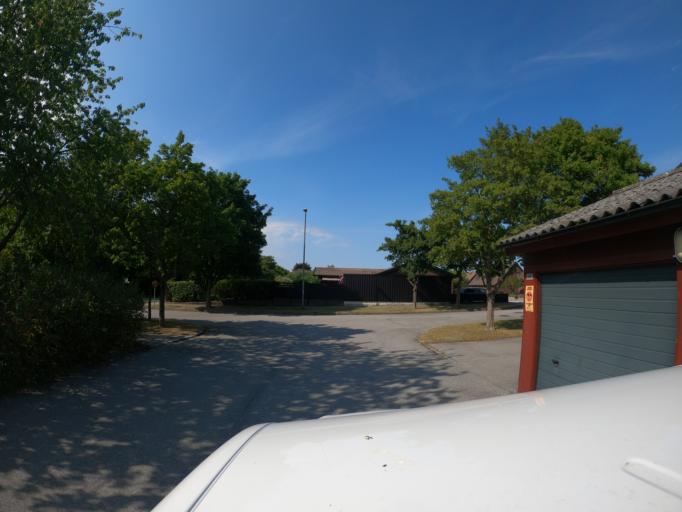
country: SE
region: Skane
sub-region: Lunds Kommun
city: Lund
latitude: 55.7277
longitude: 13.1680
